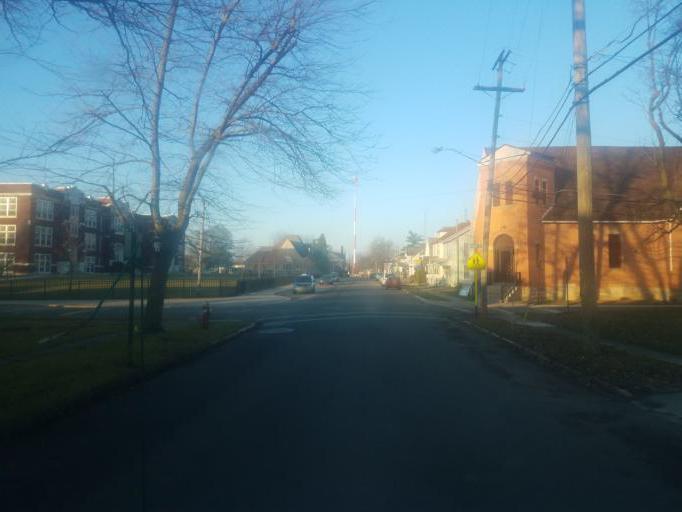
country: US
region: Ohio
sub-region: Crawford County
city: Bucyrus
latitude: 40.8048
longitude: -82.9708
